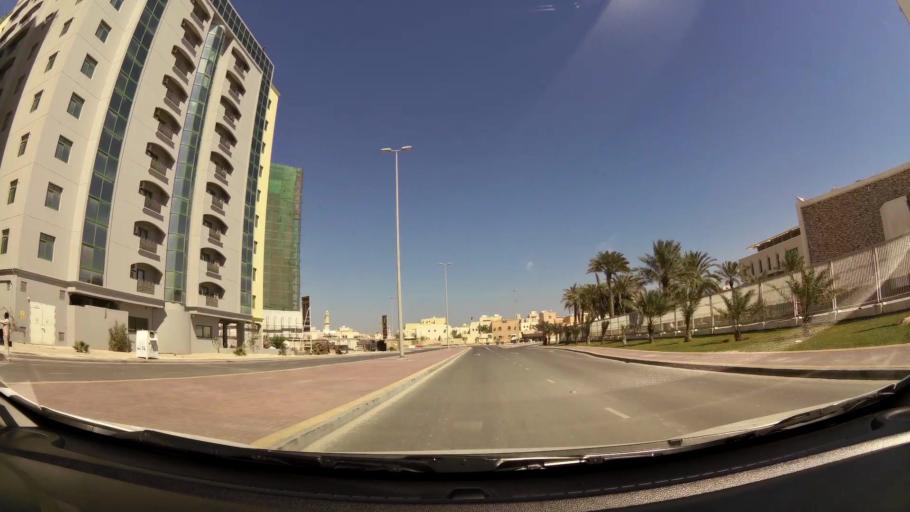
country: BH
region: Muharraq
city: Al Muharraq
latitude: 26.2654
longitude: 50.5979
